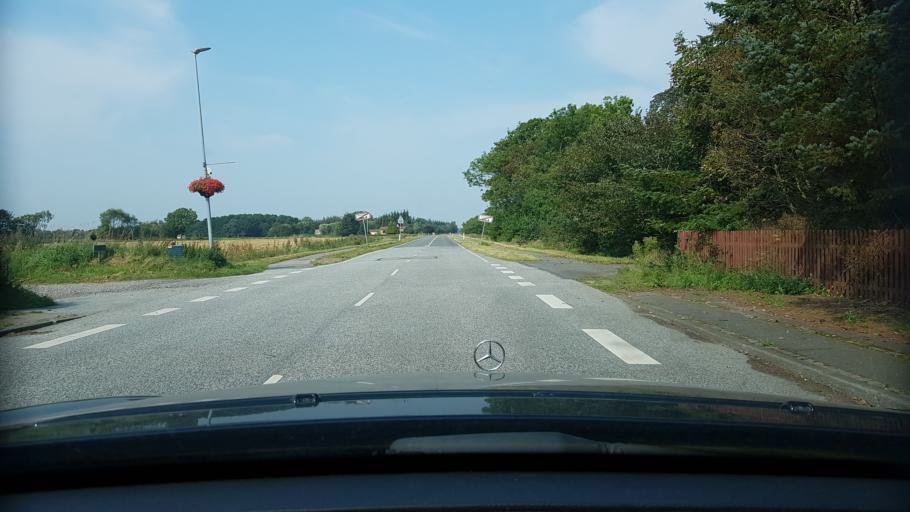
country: DK
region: North Denmark
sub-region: Alborg Kommune
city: Hals
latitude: 56.9058
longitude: 10.2531
